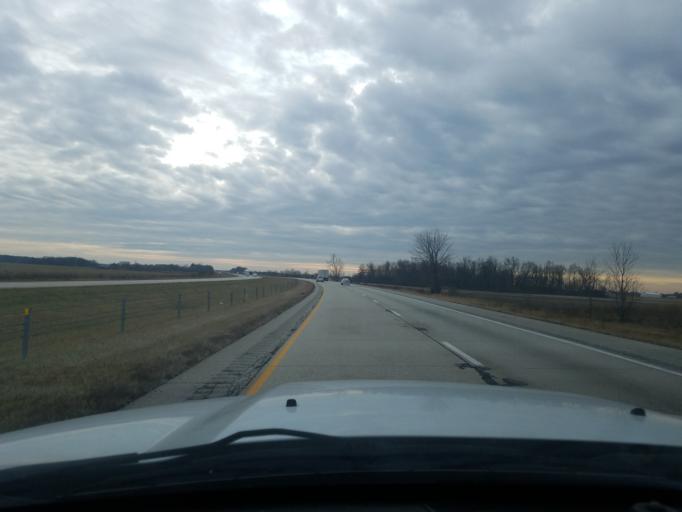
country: US
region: Indiana
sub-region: Grant County
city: Marion
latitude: 40.5916
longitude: -85.5513
